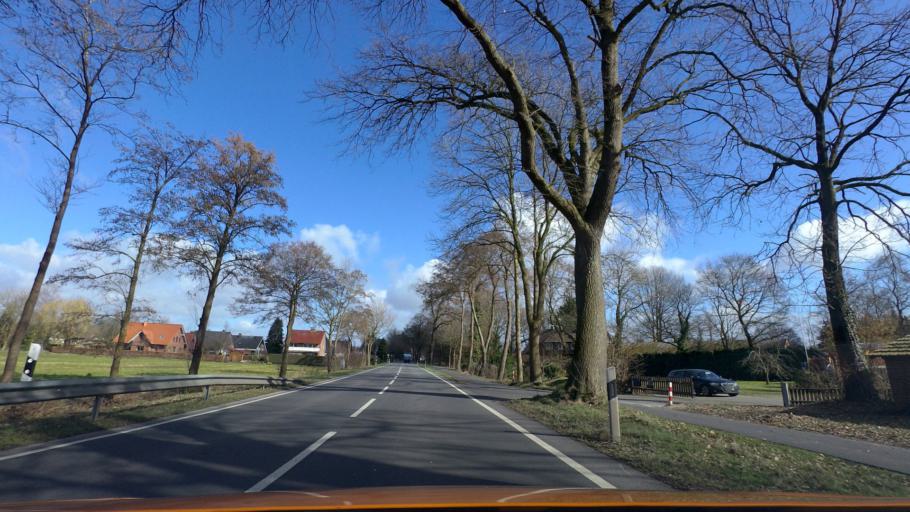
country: DE
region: Lower Saxony
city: Edewecht
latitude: 53.1142
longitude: 7.9638
